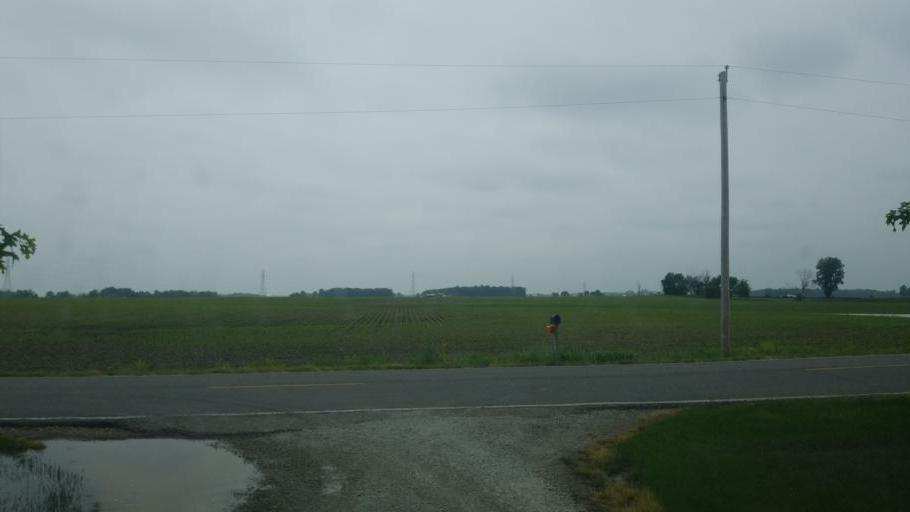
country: US
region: Indiana
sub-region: Marshall County
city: Bremen
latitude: 41.4848
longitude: -86.1177
